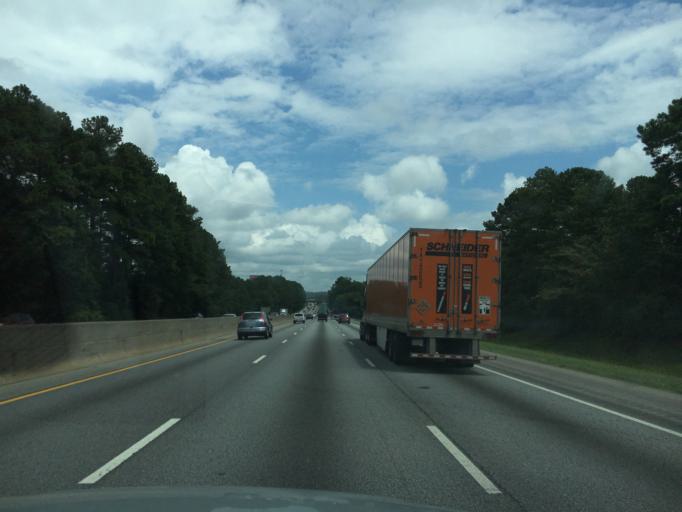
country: US
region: Georgia
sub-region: DeKalb County
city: Redan
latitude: 33.7032
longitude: -84.1572
